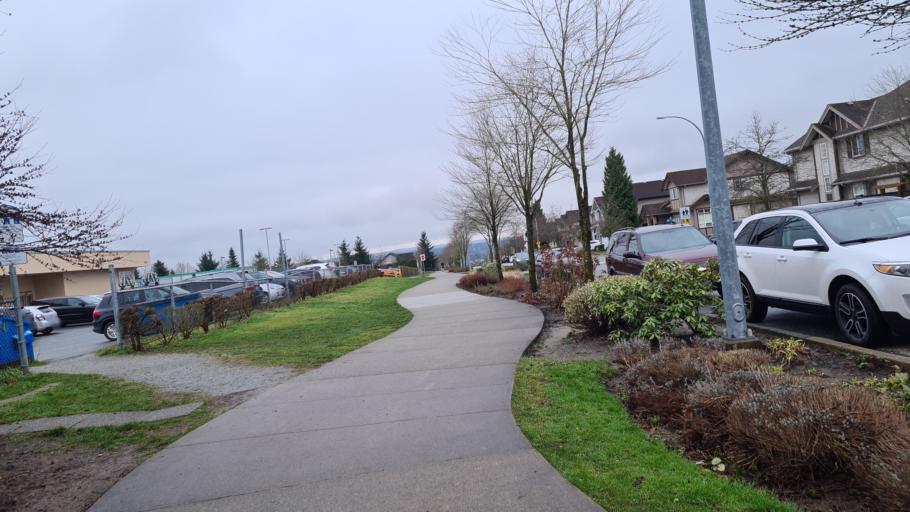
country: CA
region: British Columbia
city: Langley
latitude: 49.1324
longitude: -122.6645
